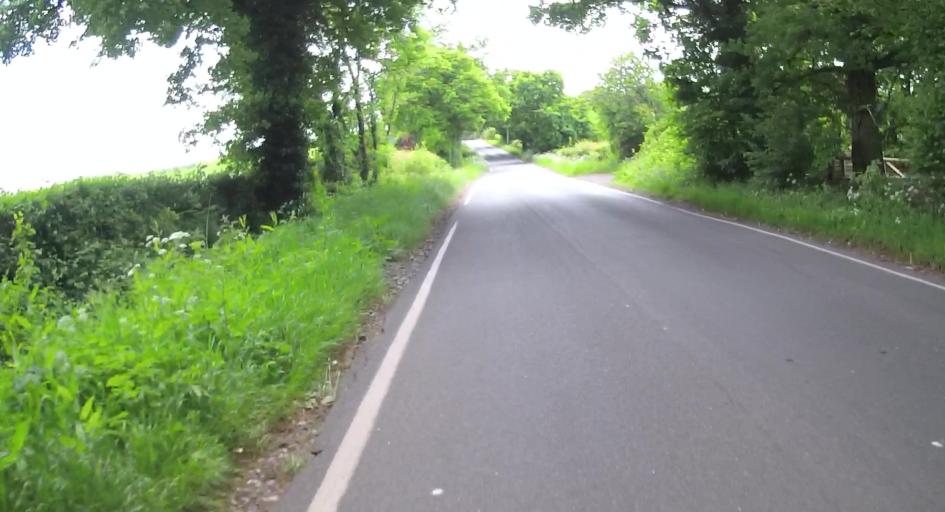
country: GB
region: England
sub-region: Surrey
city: Farnham
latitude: 51.2303
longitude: -0.8352
